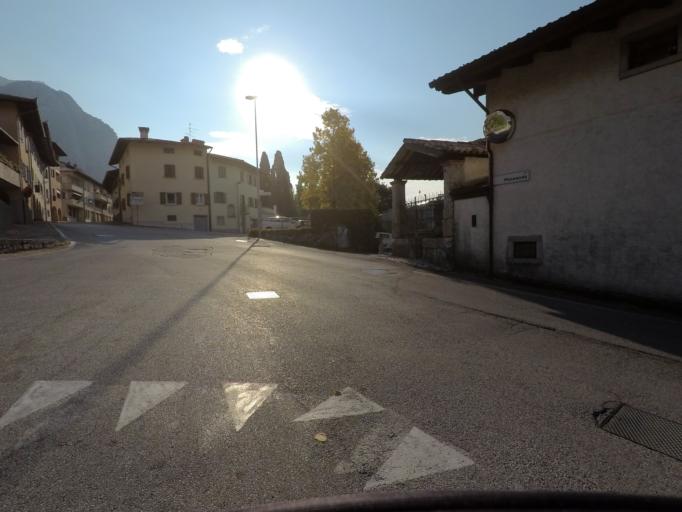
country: IT
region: Friuli Venezia Giulia
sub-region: Provincia di Udine
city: Gemona
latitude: 46.2793
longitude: 13.1345
